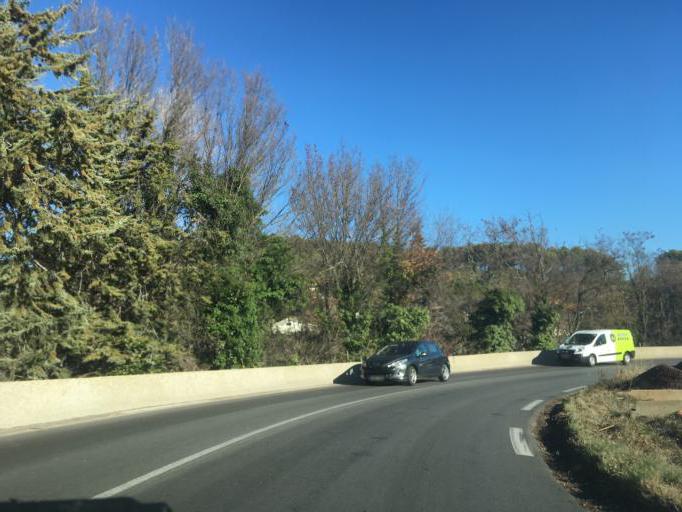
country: FR
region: Provence-Alpes-Cote d'Azur
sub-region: Departement du Var
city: Flayosc
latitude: 43.5371
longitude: 6.3976
